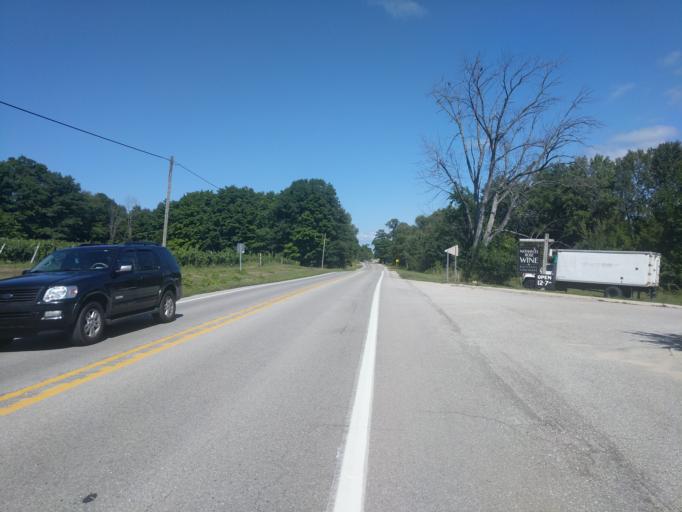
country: US
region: Michigan
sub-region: Leelanau County
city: Leland
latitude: 45.0090
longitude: -85.6190
